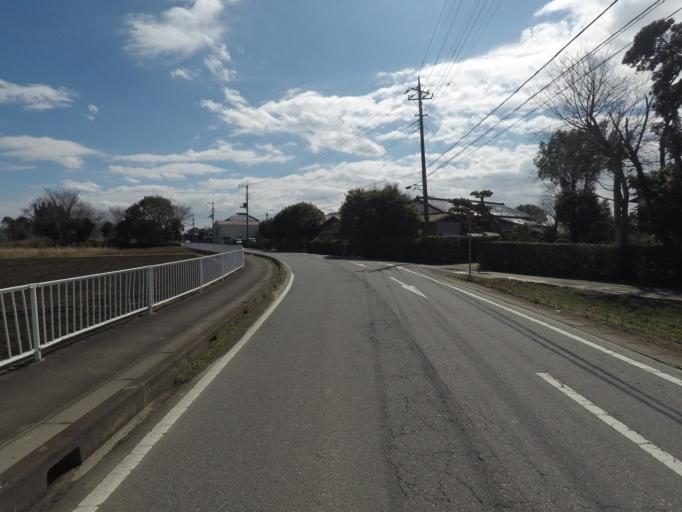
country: JP
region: Ibaraki
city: Moriya
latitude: 35.9575
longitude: 140.0541
